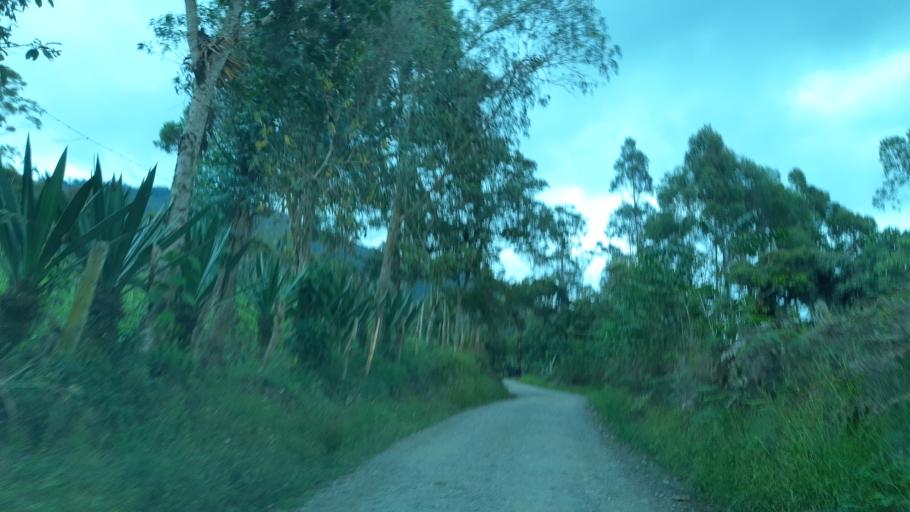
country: CO
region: Boyaca
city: Garagoa
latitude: 5.1228
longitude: -73.3443
